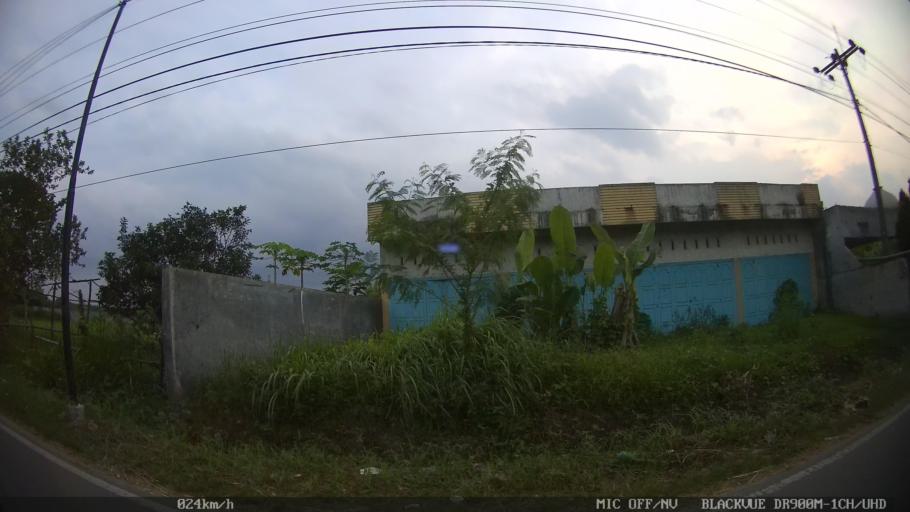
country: ID
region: North Sumatra
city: Sunggal
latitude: 3.5816
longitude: 98.6028
